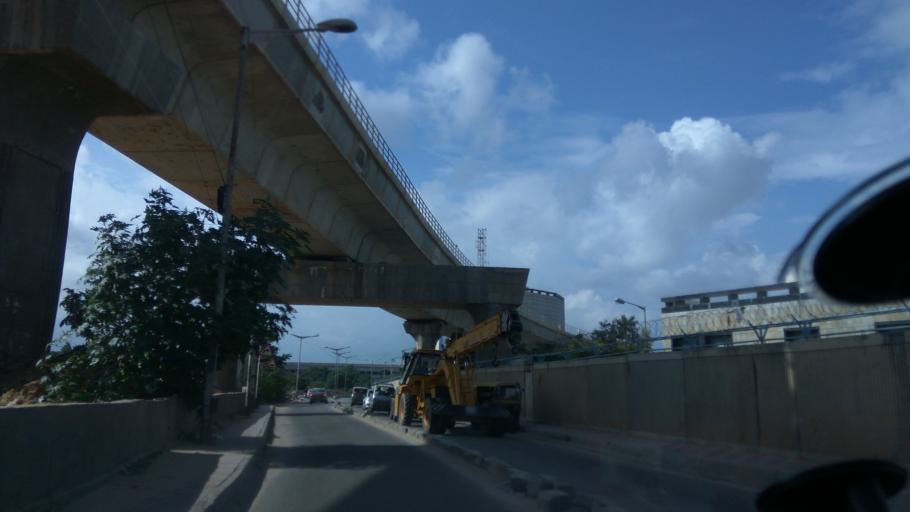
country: IN
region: Karnataka
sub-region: Bangalore Urban
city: Bangalore
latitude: 12.9885
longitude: 77.6487
